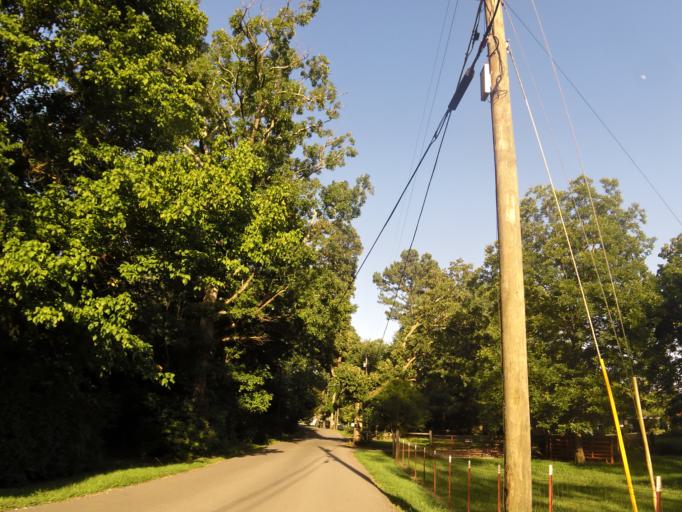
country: US
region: Tennessee
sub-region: Knox County
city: Knoxville
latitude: 35.9167
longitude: -83.9424
